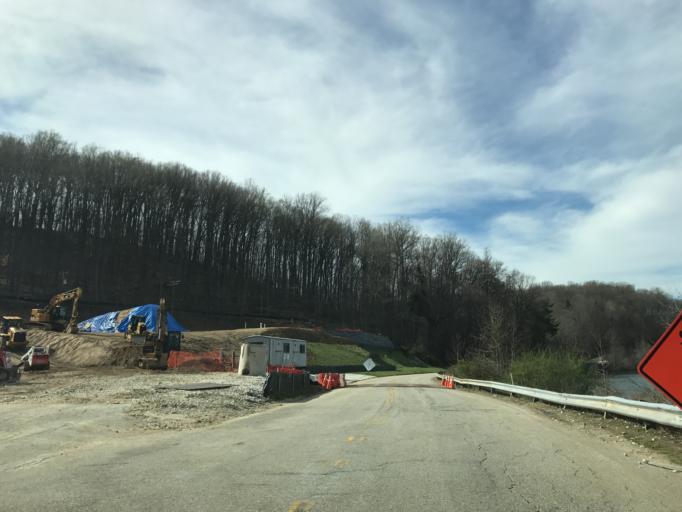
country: US
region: Maryland
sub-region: Baltimore County
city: Carney
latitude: 39.4252
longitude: -76.5439
